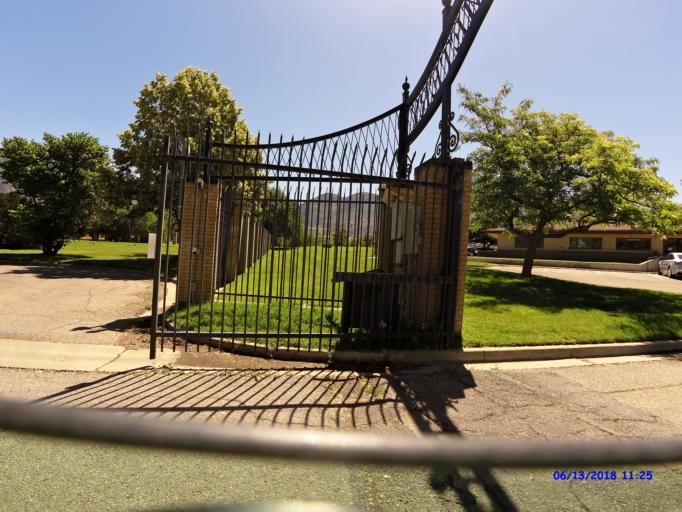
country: US
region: Utah
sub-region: Weber County
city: Ogden
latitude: 41.2342
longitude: -111.9601
